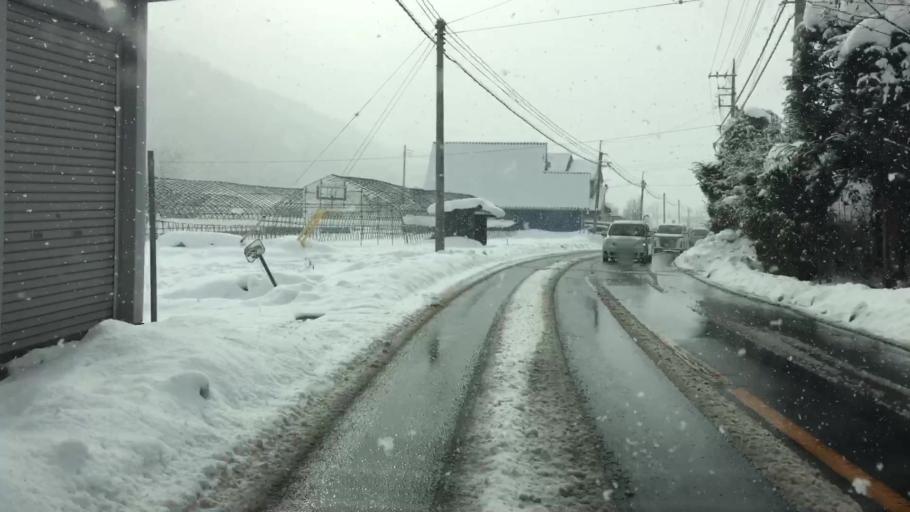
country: JP
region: Gunma
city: Numata
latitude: 36.7045
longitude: 139.0657
